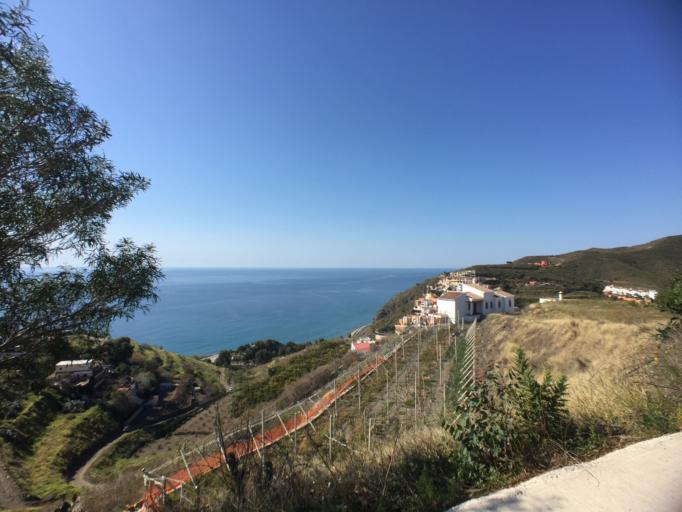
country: ES
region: Andalusia
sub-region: Provincia de Malaga
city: Nerja
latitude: 36.7463
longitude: -3.9092
